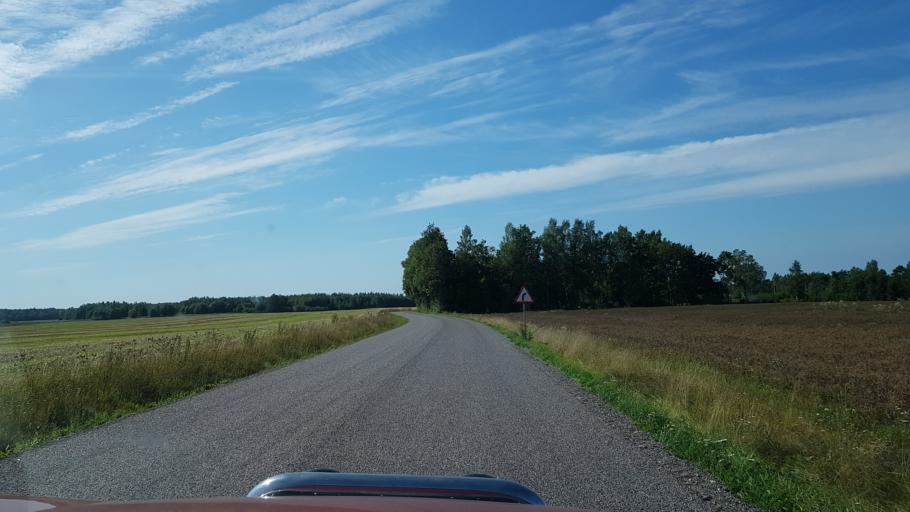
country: EE
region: Tartu
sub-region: Puhja vald
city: Puhja
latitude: 58.2548
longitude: 26.2863
